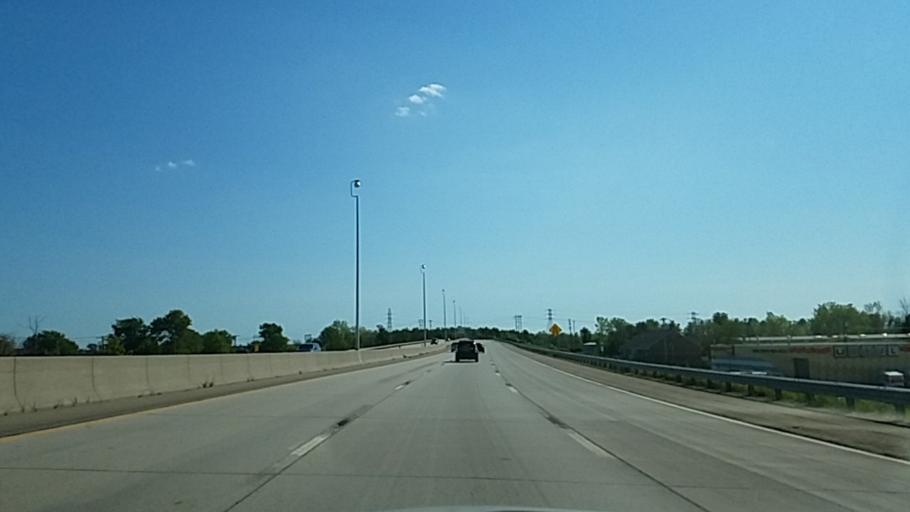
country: US
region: New York
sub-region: Erie County
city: Tonawanda
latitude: 42.9792
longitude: -78.9102
